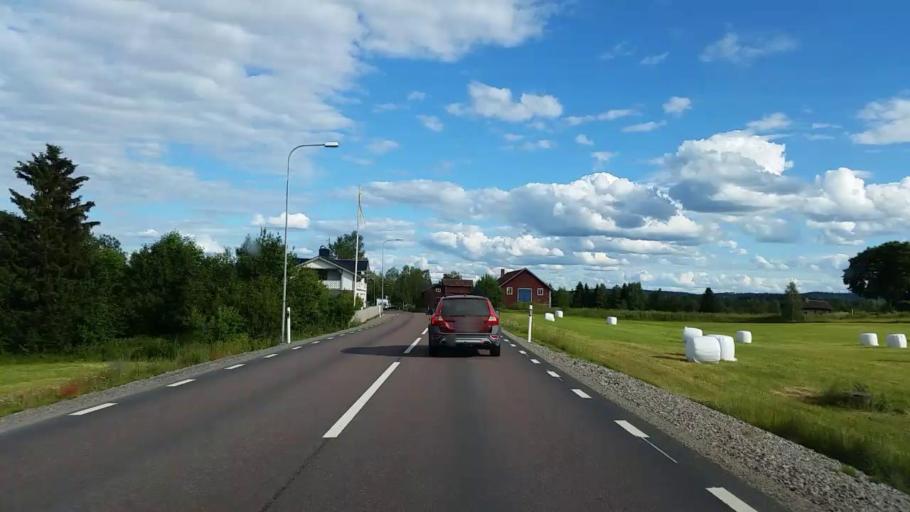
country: SE
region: Gaevleborg
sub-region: Ljusdals Kommun
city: Ljusdal
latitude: 61.8492
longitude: 15.9962
